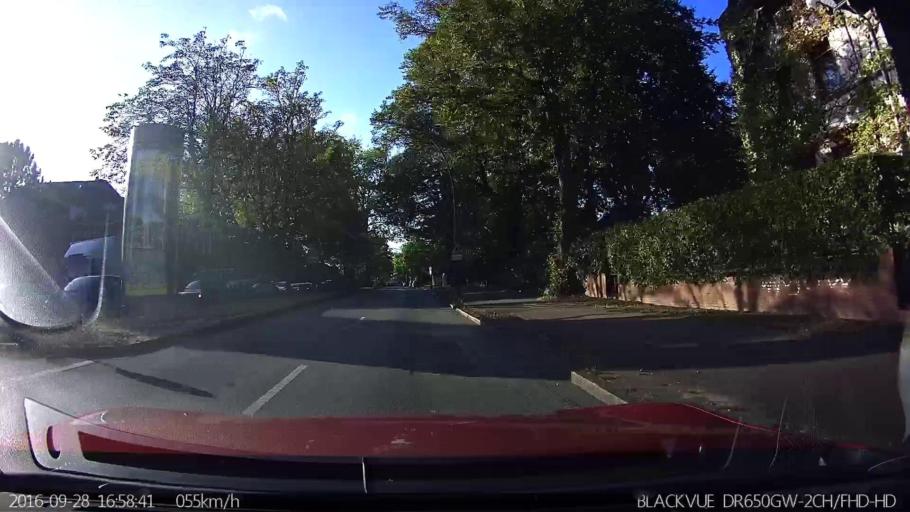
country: DE
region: Hamburg
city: Altona
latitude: 53.5658
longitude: 9.8959
